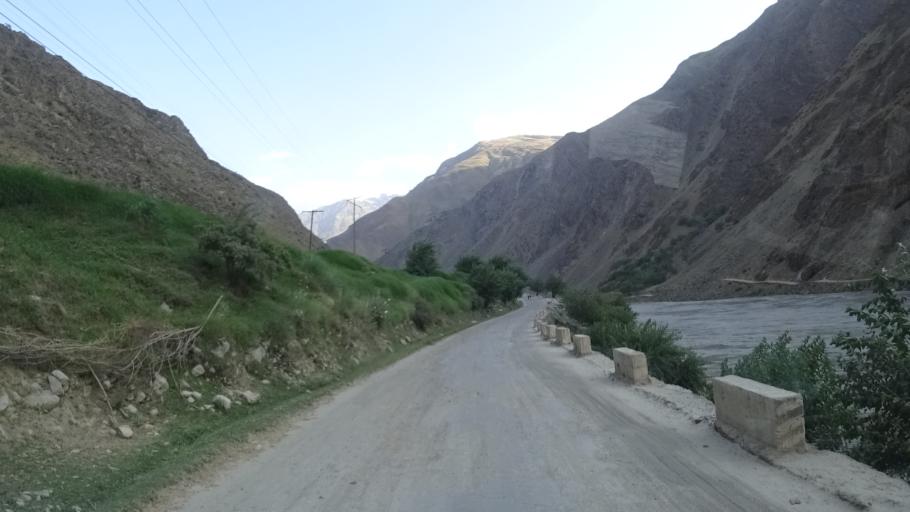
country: AF
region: Badakhshan
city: Maymay
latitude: 38.4598
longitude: 71.0322
